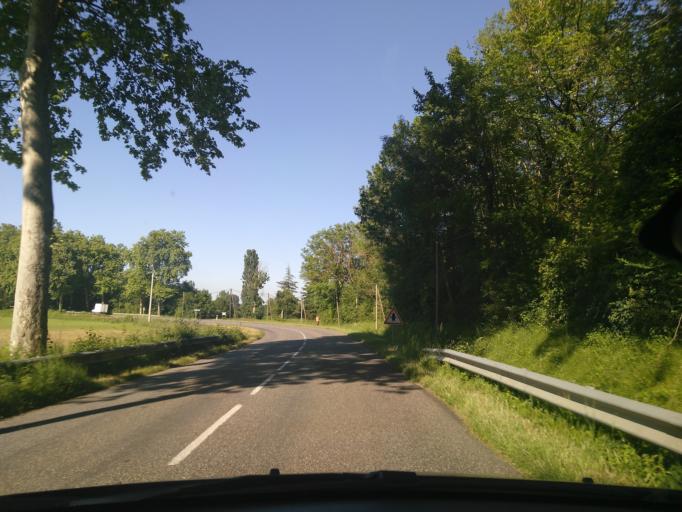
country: FR
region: Midi-Pyrenees
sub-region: Departement du Gers
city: Aubiet
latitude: 43.5328
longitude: 0.7667
